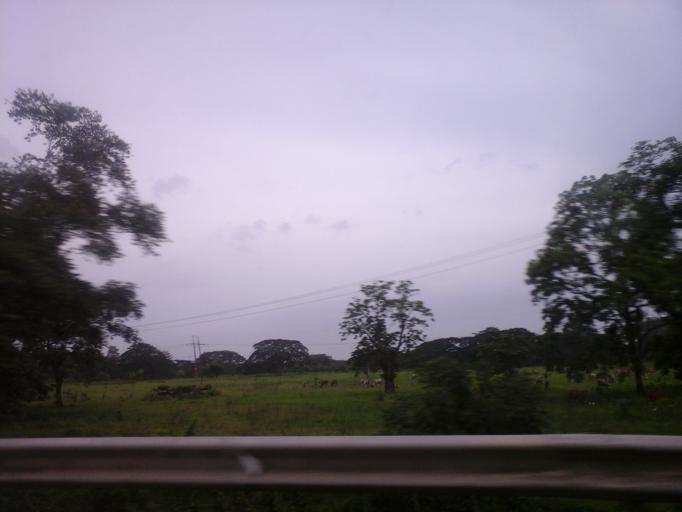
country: CO
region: Bolivar
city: San Pablo
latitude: 10.1368
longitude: -75.2718
